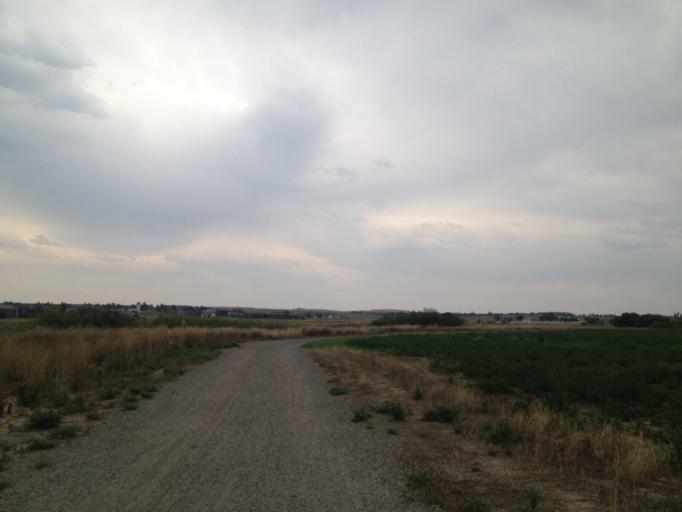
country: US
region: Colorado
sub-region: Boulder County
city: Erie
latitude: 40.0150
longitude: -105.0513
